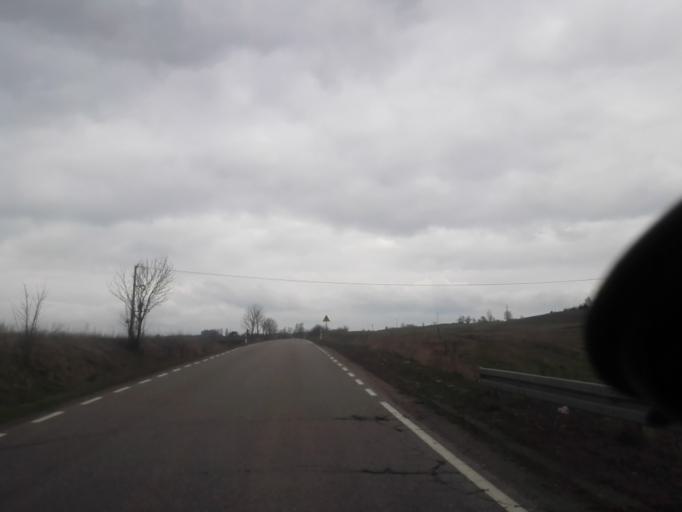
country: PL
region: Podlasie
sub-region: Suwalki
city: Suwalki
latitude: 54.2273
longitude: 22.9121
